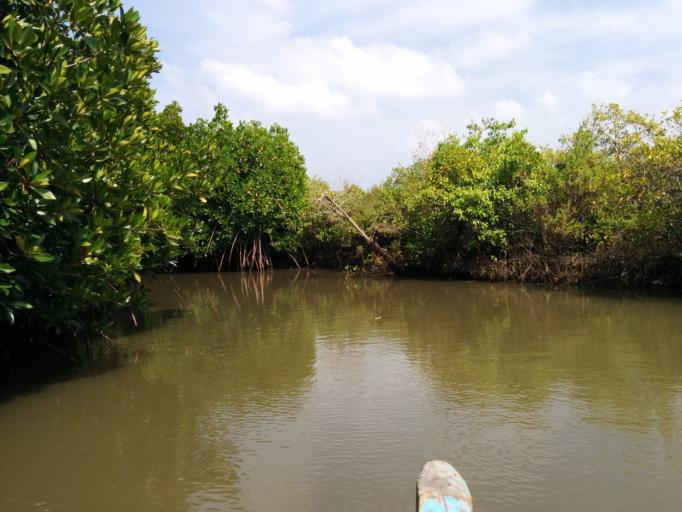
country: IN
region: Tamil Nadu
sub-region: Cuddalore
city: Annamalainagar
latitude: 11.4267
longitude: 79.7918
